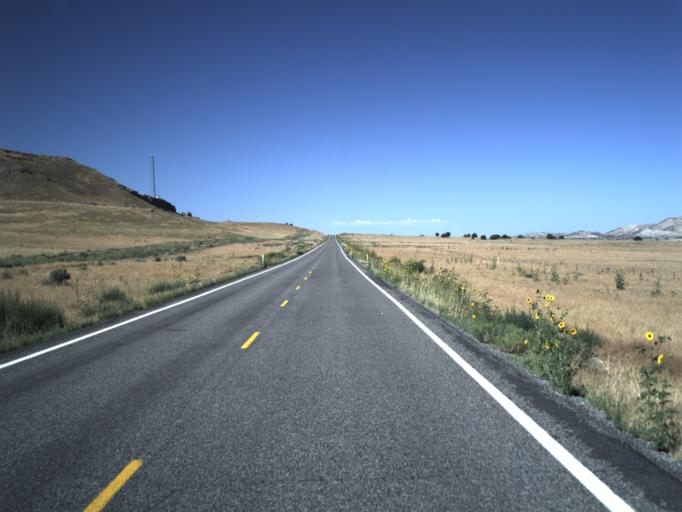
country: US
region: Utah
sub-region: Millard County
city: Delta
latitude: 39.6573
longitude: -112.2854
